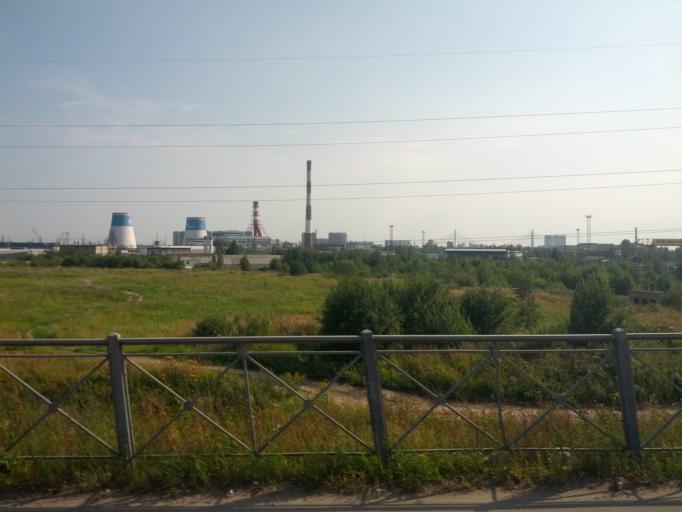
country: RU
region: Leningrad
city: Rybatskoye
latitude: 59.8854
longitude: 30.4958
